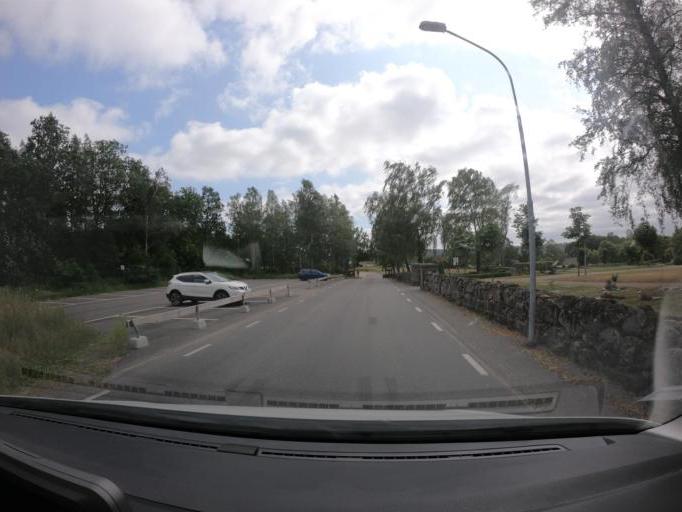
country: SE
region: Skane
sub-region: Hassleholms Kommun
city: Tormestorp
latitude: 56.1585
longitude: 13.6261
